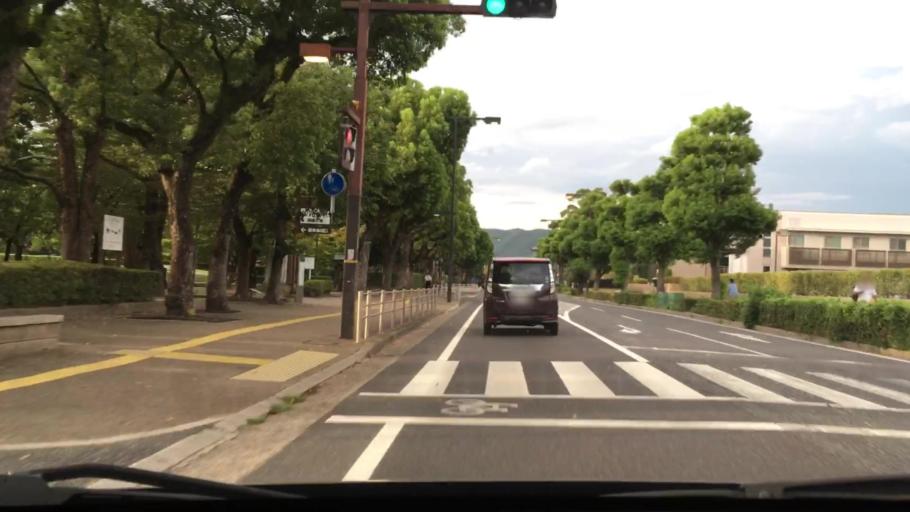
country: JP
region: Hyogo
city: Himeji
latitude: 34.8381
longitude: 134.6971
